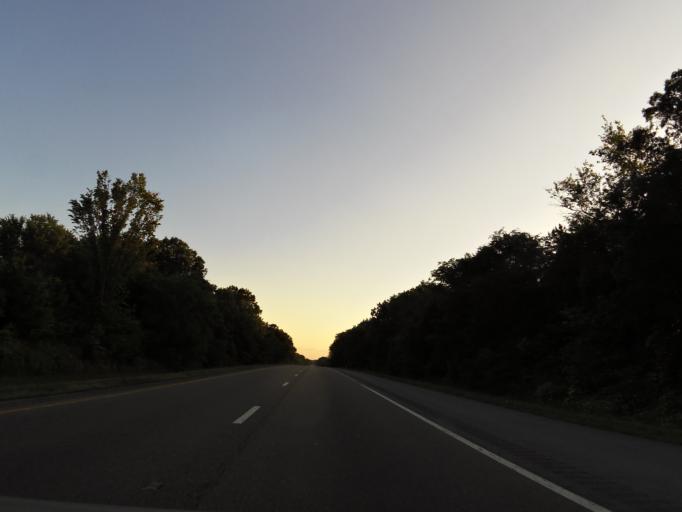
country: US
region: Tennessee
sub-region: Greene County
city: Mosheim
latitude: 36.3002
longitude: -82.8782
